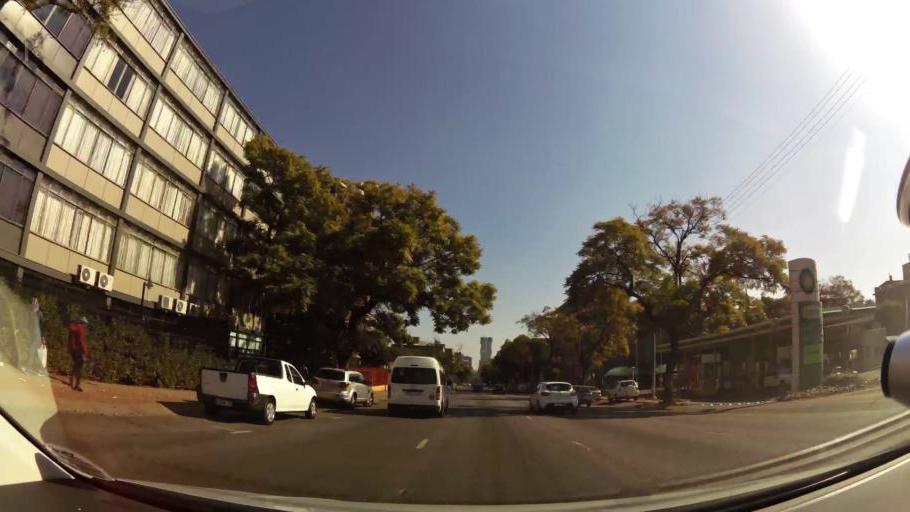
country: ZA
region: Gauteng
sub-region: City of Tshwane Metropolitan Municipality
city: Pretoria
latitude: -25.7465
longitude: 28.2088
